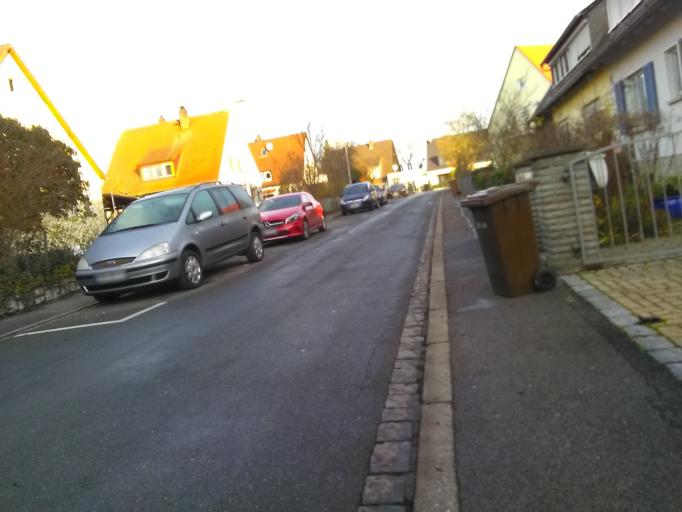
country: DE
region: Bavaria
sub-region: Upper Franconia
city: Bamberg
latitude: 49.8776
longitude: 10.8796
